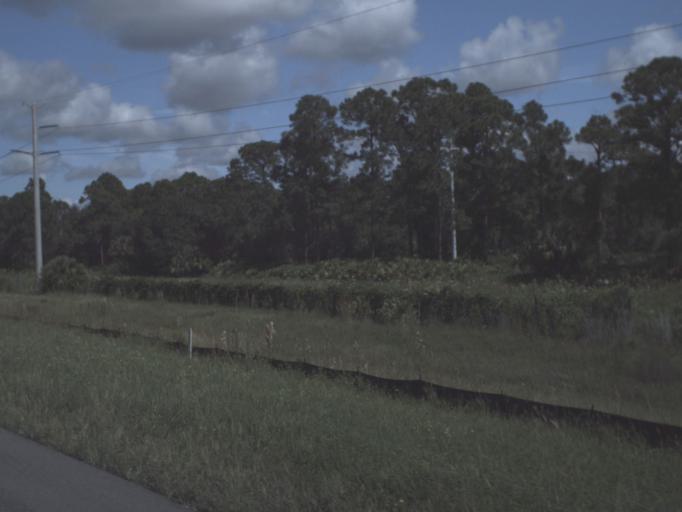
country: US
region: Florida
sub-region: Charlotte County
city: Port Charlotte
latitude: 27.0577
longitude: -82.0822
